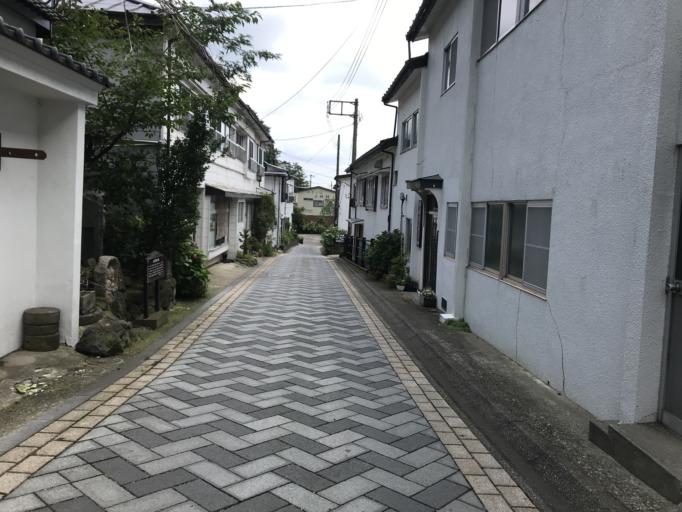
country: JP
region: Tochigi
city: Kuroiso
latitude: 37.0979
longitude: 140.0012
